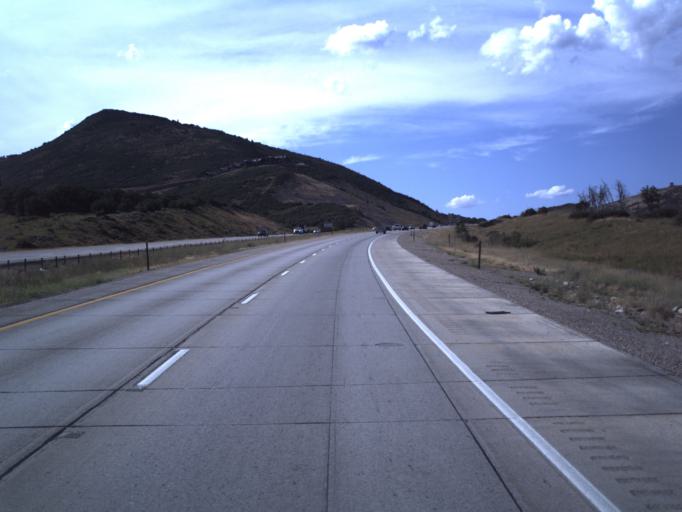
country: US
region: Utah
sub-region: Summit County
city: Park City
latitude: 40.6322
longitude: -111.4477
